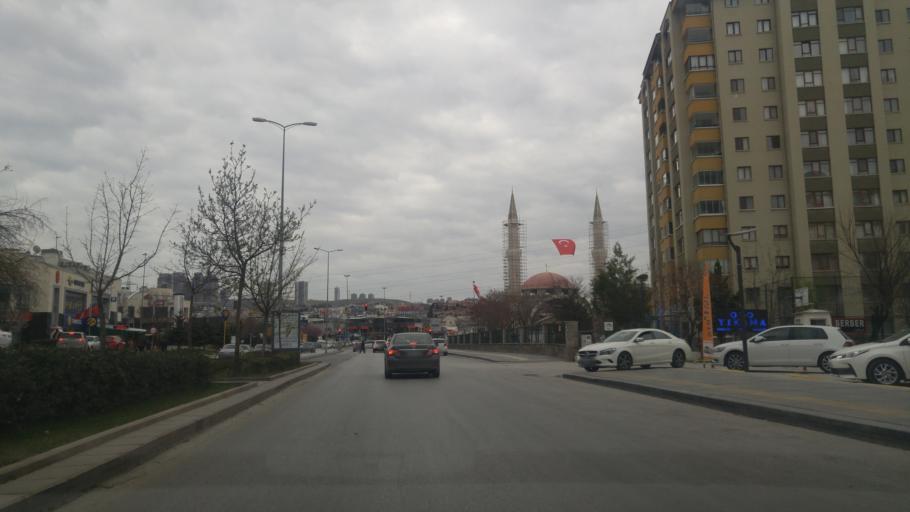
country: TR
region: Ankara
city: Etimesgut
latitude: 39.8750
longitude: 32.6874
